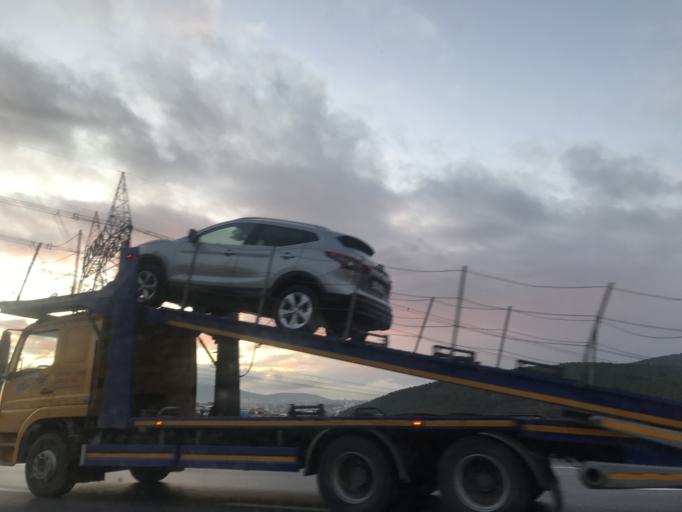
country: TR
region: Istanbul
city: Sultanbeyli
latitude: 40.9589
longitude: 29.3186
